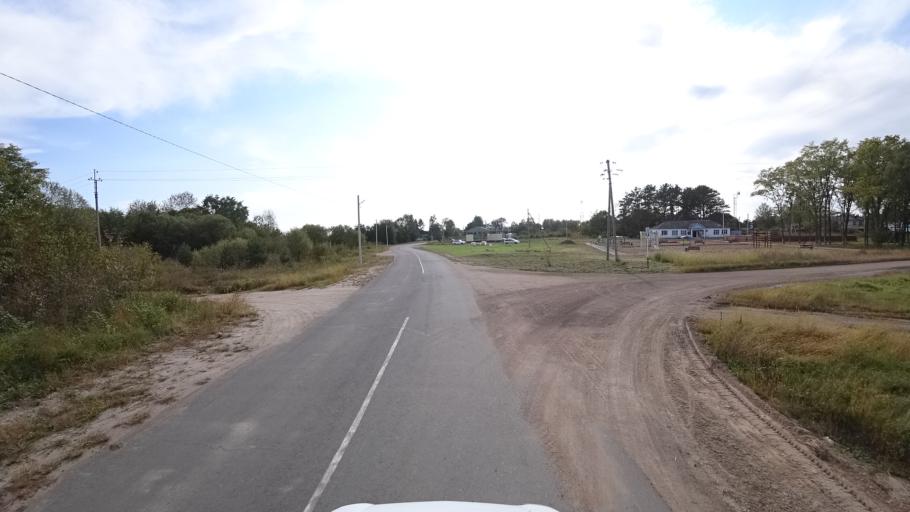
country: RU
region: Amur
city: Arkhara
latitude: 49.3632
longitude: 130.1227
